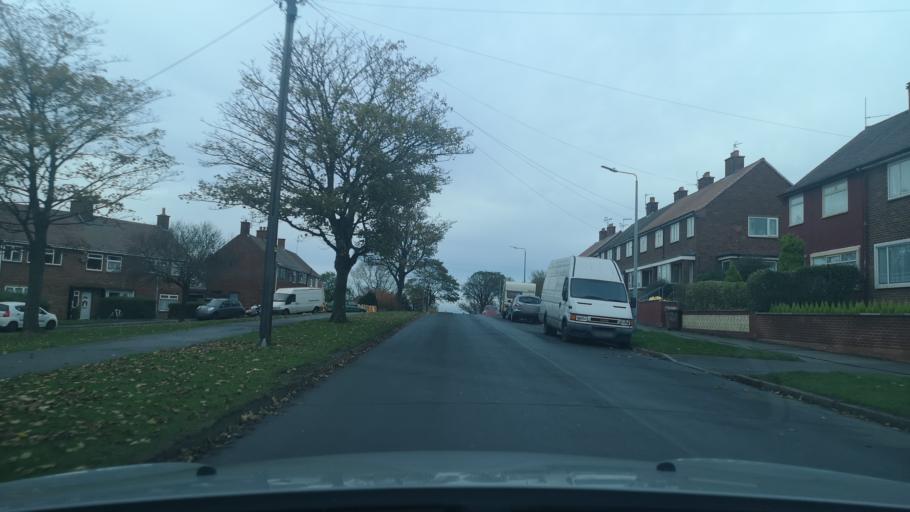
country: GB
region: England
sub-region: East Riding of Yorkshire
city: Hornsea
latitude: 53.9046
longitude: -0.1680
